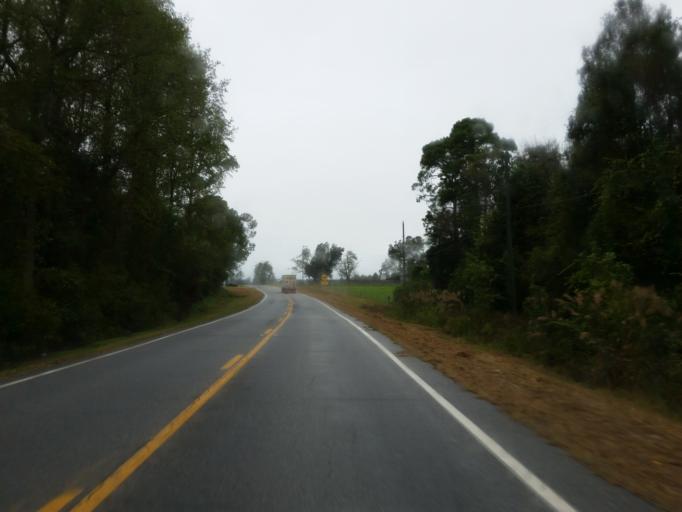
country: US
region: Georgia
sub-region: Berrien County
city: Nashville
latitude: 31.1160
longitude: -83.3076
